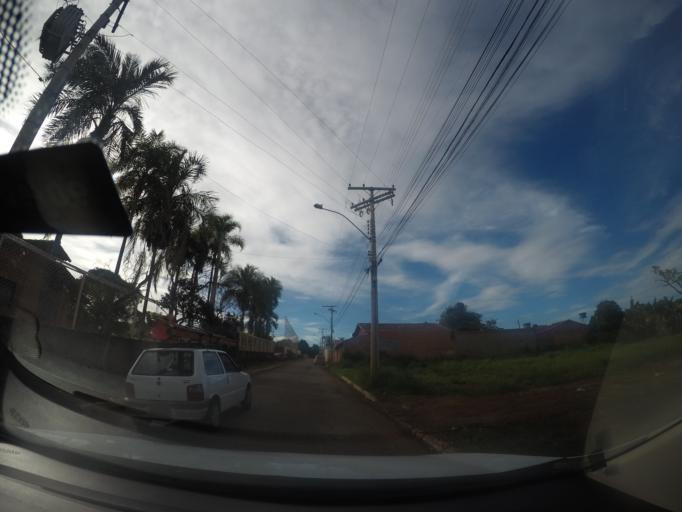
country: BR
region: Goias
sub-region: Goiania
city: Goiania
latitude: -16.6327
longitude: -49.3527
